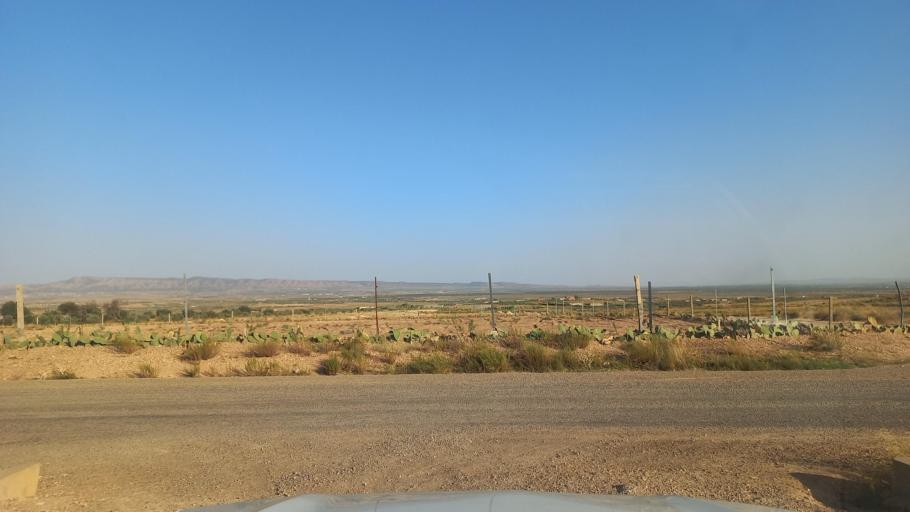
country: TN
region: Al Qasrayn
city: Sbiba
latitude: 35.3683
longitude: 9.0089
